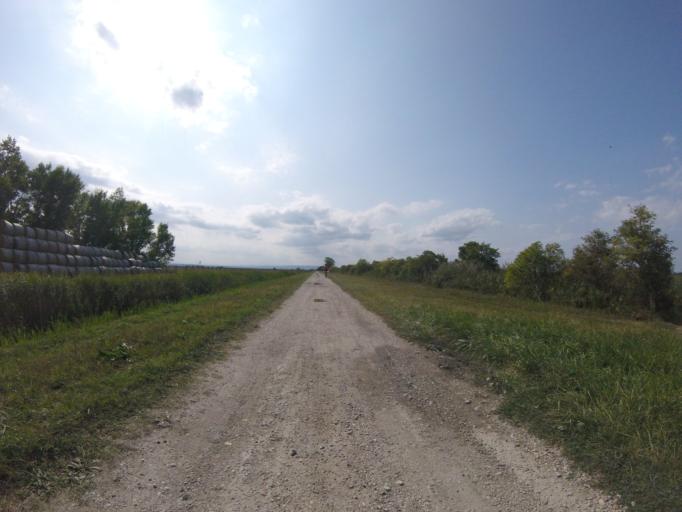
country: HU
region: Gyor-Moson-Sopron
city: Fertod
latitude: 47.6784
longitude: 16.8469
